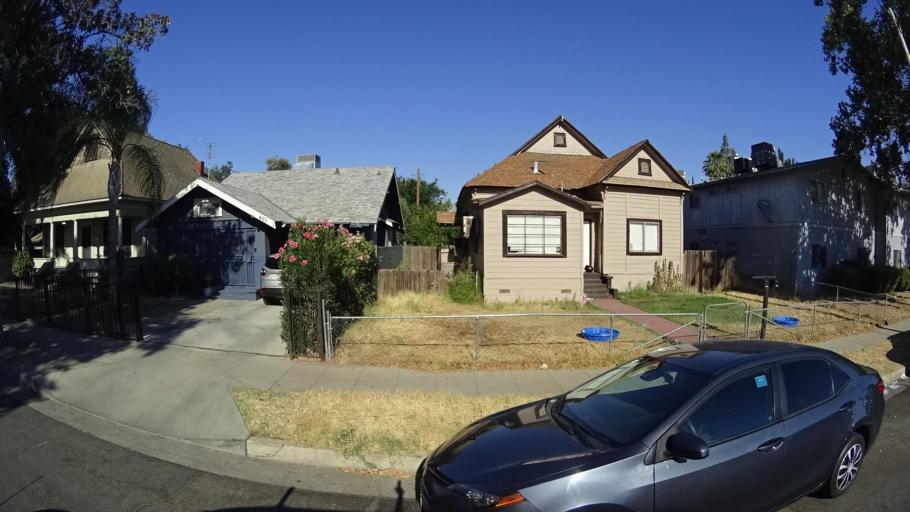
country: US
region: California
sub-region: Fresno County
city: Fresno
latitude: 36.7487
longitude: -119.7934
